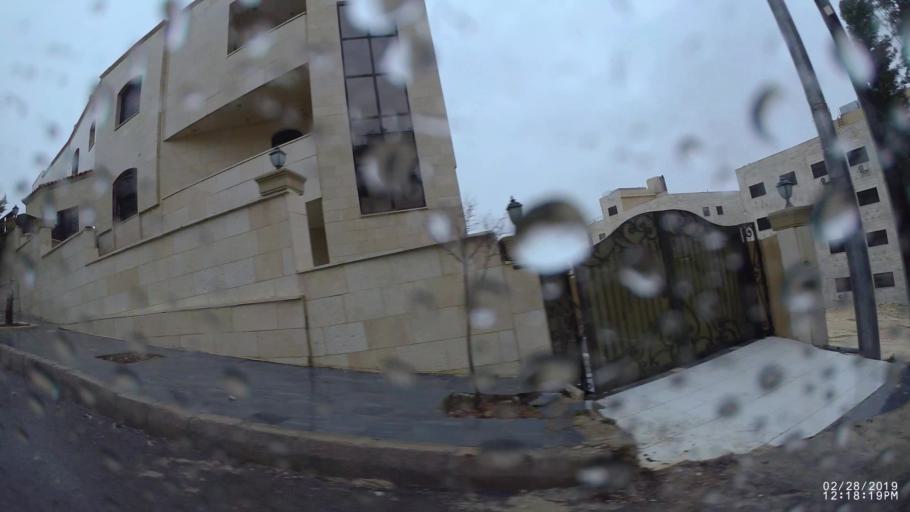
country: JO
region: Amman
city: Al Jubayhah
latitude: 32.0255
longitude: 35.8864
